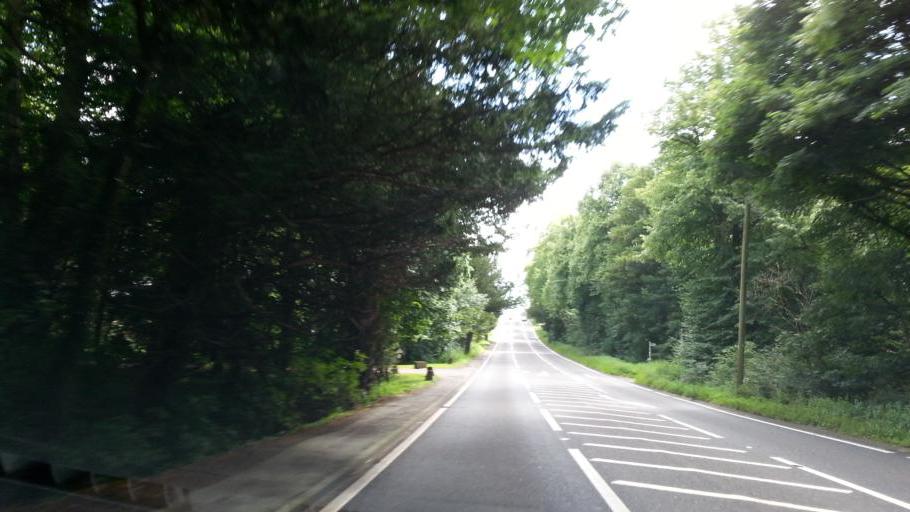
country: GB
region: England
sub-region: Nottinghamshire
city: Edwinstowe
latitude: 53.1732
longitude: -1.0434
